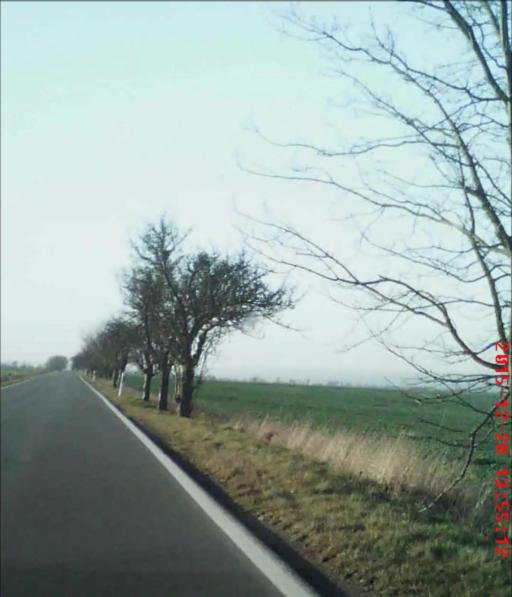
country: DE
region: Thuringia
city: Schmiedehausen
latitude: 51.0648
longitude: 11.6486
